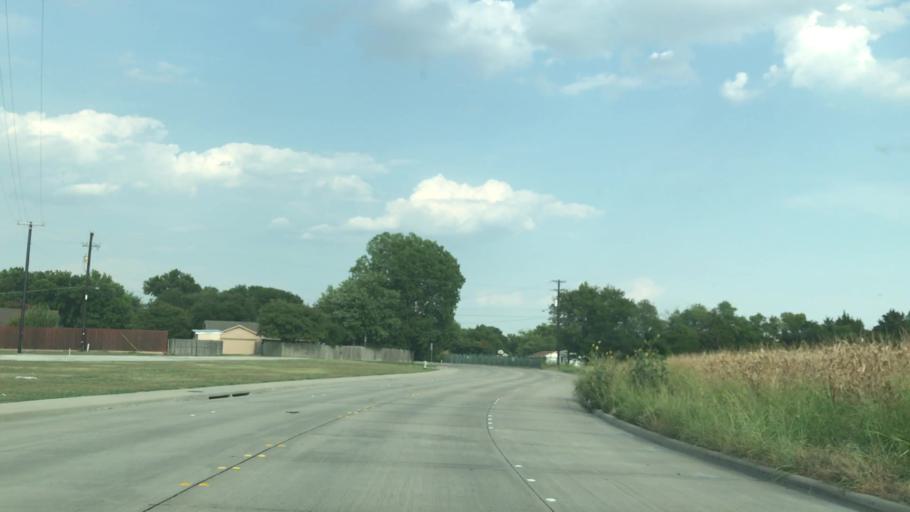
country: US
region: Texas
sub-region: Rockwall County
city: Rockwall
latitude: 32.9258
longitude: -96.4284
